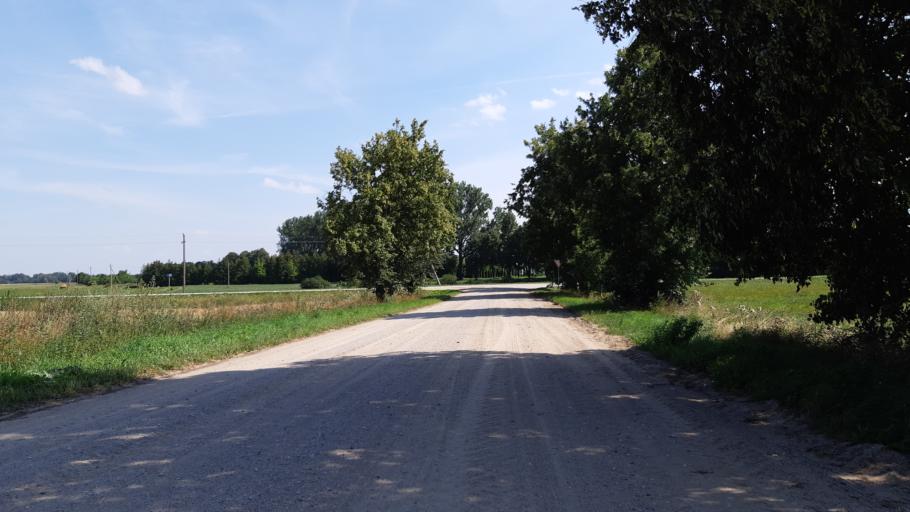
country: LT
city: Virbalis
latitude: 54.6343
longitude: 22.8264
